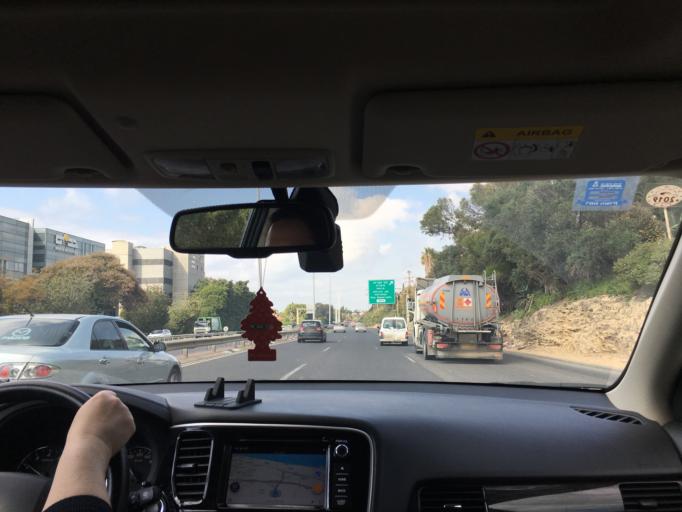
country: IL
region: Tel Aviv
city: Herzliyya
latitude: 32.1664
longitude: 34.8134
